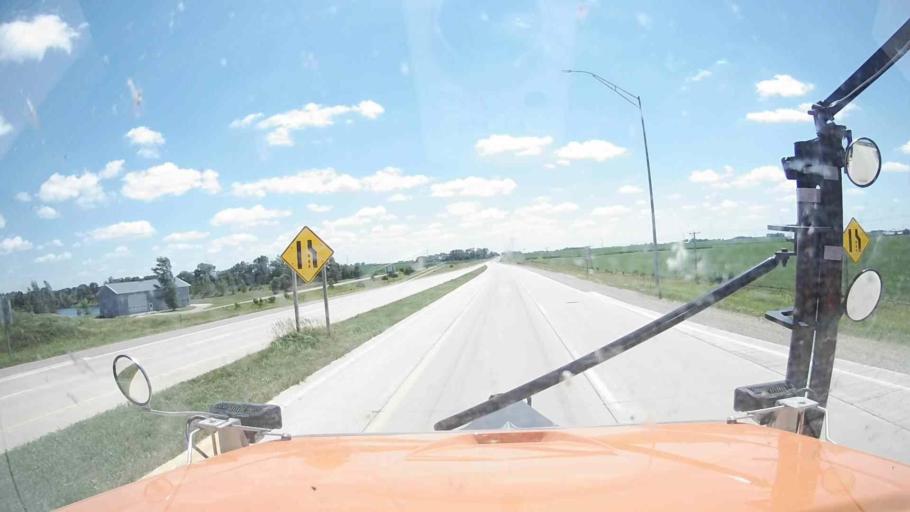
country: US
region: Iowa
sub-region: Cerro Gordo County
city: Mason City
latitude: 43.1032
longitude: -93.2015
